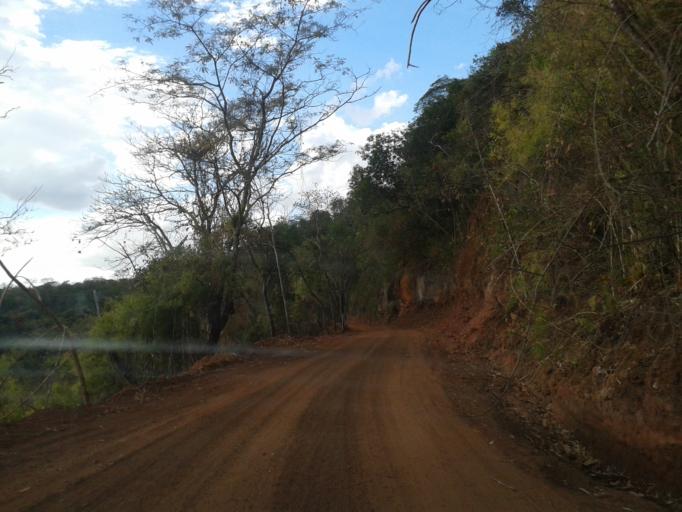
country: BR
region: Minas Gerais
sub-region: Santa Vitoria
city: Santa Vitoria
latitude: -19.1989
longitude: -49.8813
